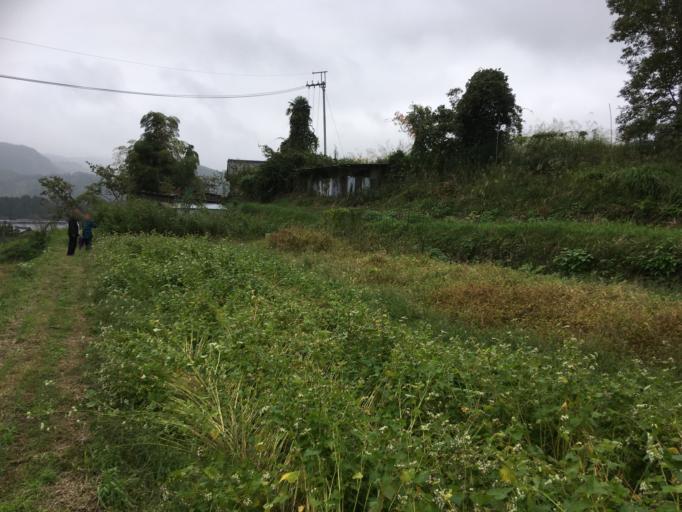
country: JP
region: Nara
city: Haibara-akanedai
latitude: 34.5657
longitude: 136.0097
